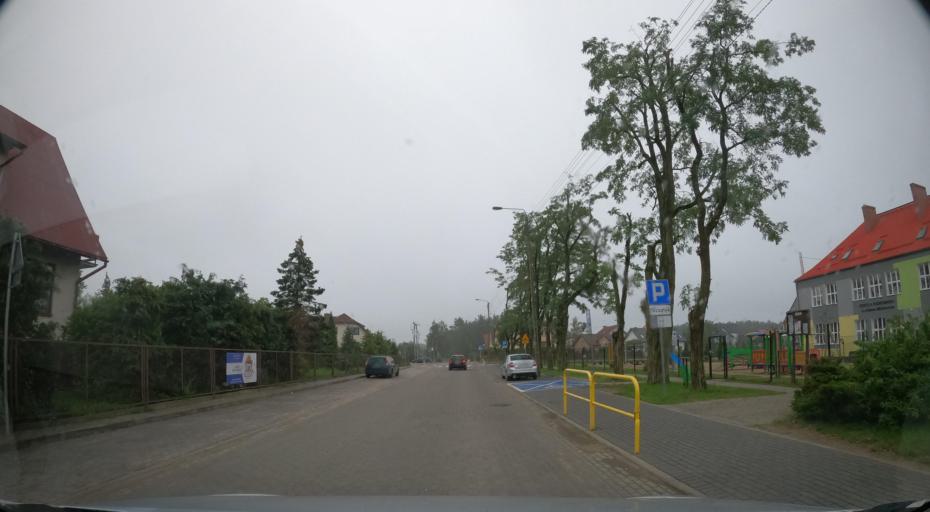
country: PL
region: Pomeranian Voivodeship
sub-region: Powiat kartuski
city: Chwaszczyno
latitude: 54.4400
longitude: 18.4185
